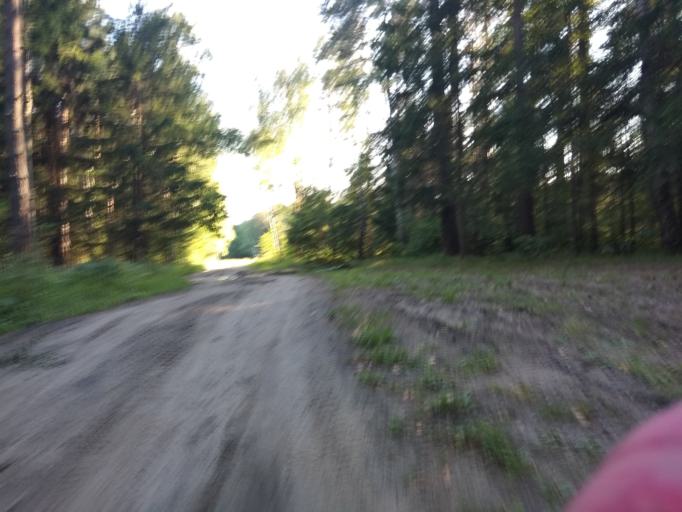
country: RU
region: Moskovskaya
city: Misheronskiy
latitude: 55.7255
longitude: 39.7521
